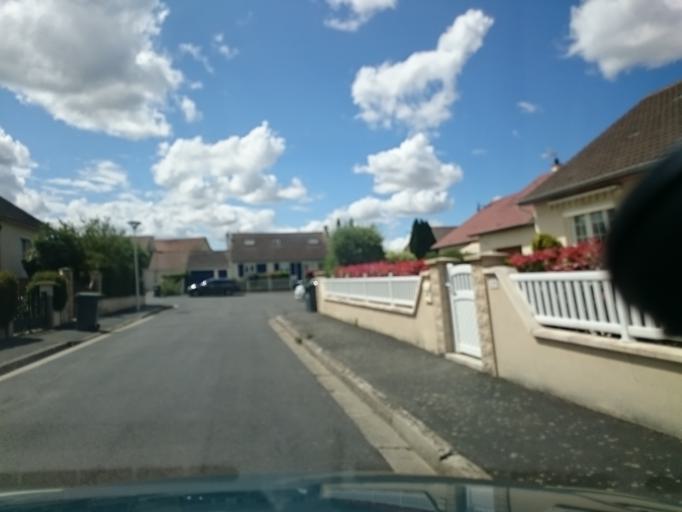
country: FR
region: Lower Normandy
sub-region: Departement du Calvados
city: Ifs
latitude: 49.1392
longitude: -0.3567
